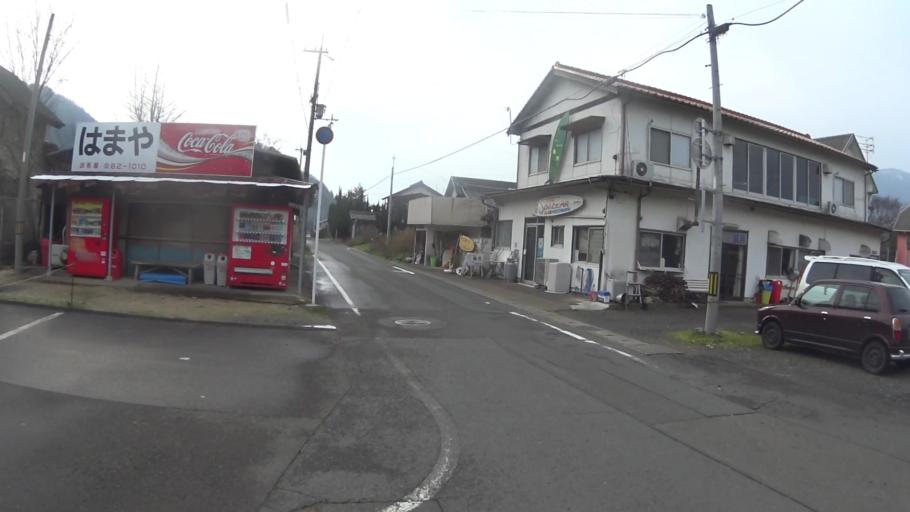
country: JP
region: Kyoto
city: Maizuru
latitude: 35.5140
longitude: 135.2969
